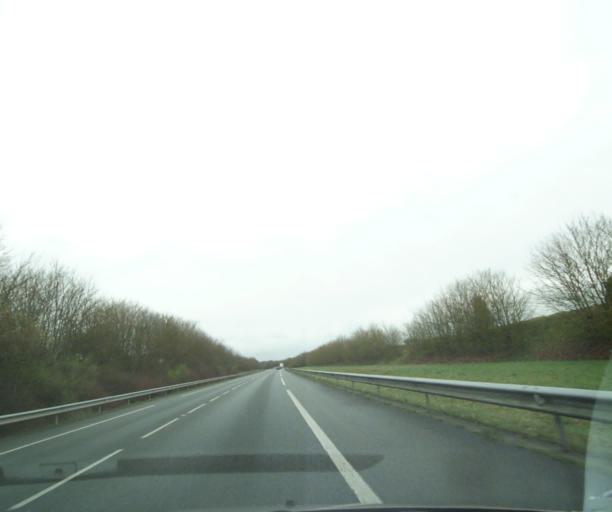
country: FR
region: Picardie
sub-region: Departement de l'Oise
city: Noyon
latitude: 49.5715
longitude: 3.0254
